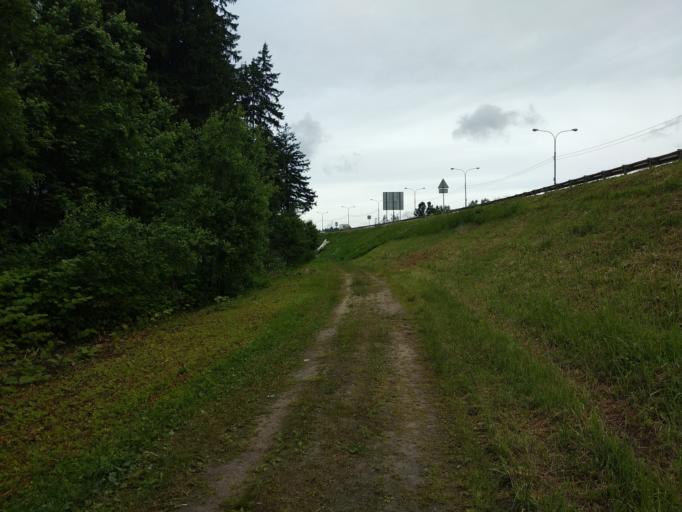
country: RU
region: Moskovskaya
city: Nekrasovskiy
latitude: 56.1223
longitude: 37.5214
